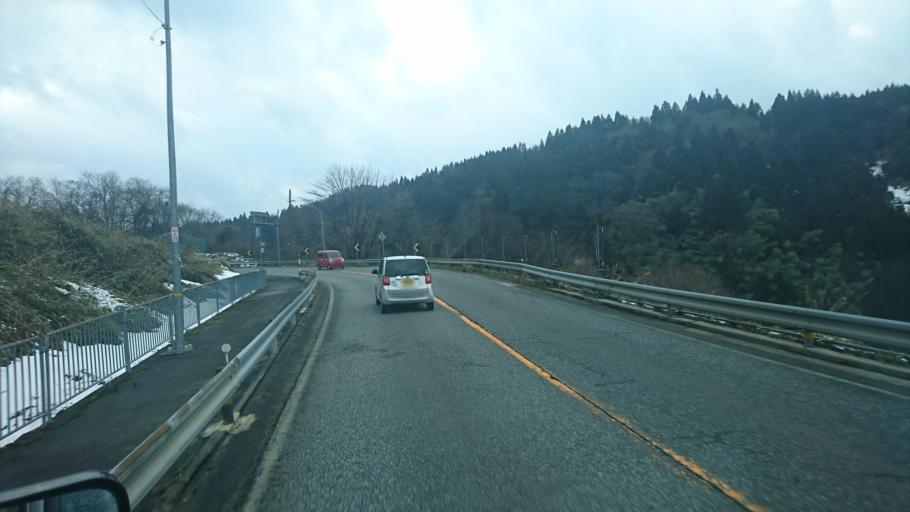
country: JP
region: Hyogo
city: Toyooka
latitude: 35.4298
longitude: 134.6006
